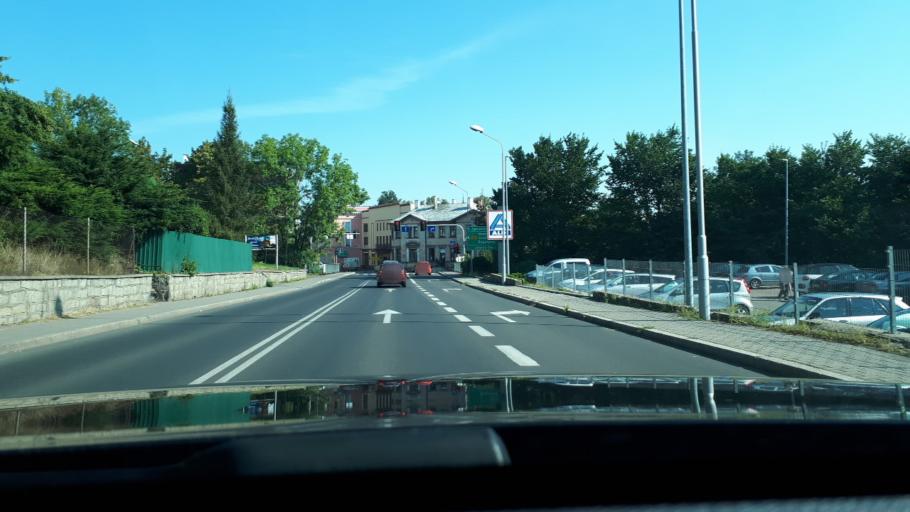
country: PL
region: Lower Silesian Voivodeship
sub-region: Powiat lubanski
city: Luban
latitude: 51.1162
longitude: 15.2894
